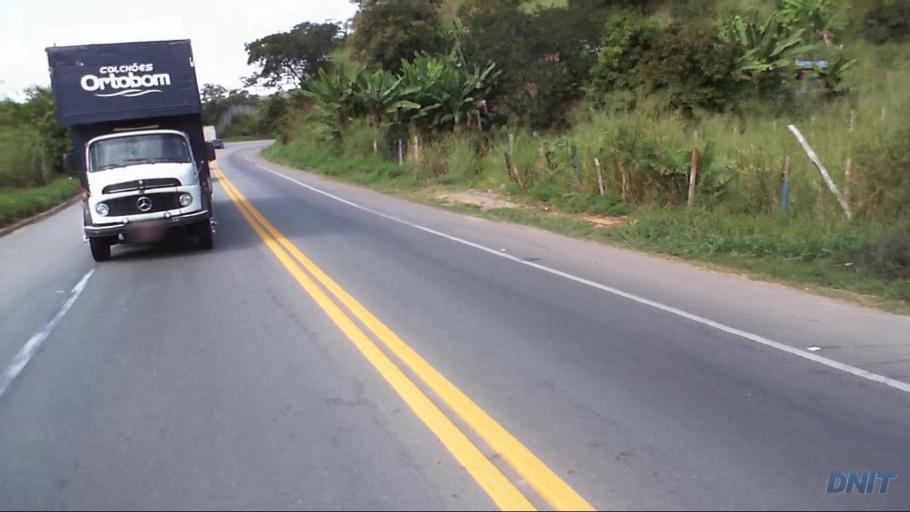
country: BR
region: Minas Gerais
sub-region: Santa Luzia
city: Santa Luzia
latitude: -19.8225
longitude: -43.8171
